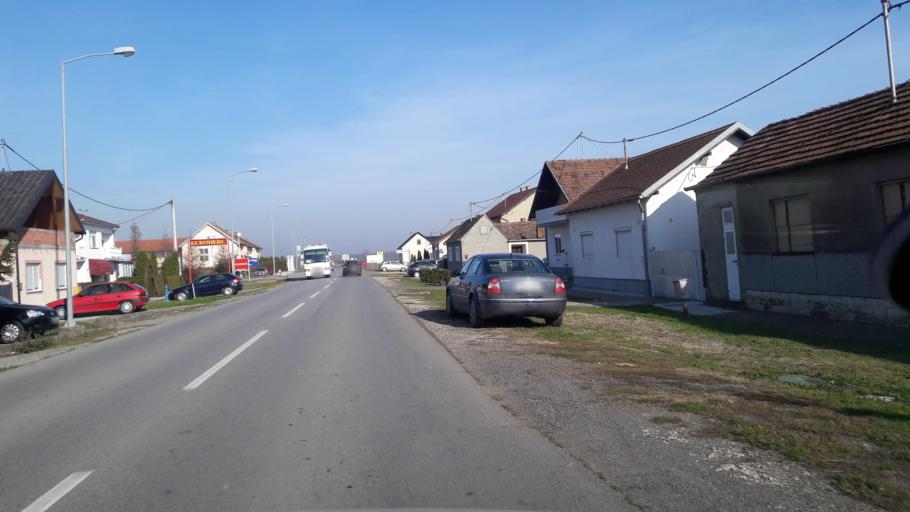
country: HR
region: Vukovarsko-Srijemska
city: Zupanja
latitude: 45.0914
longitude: 18.7015
